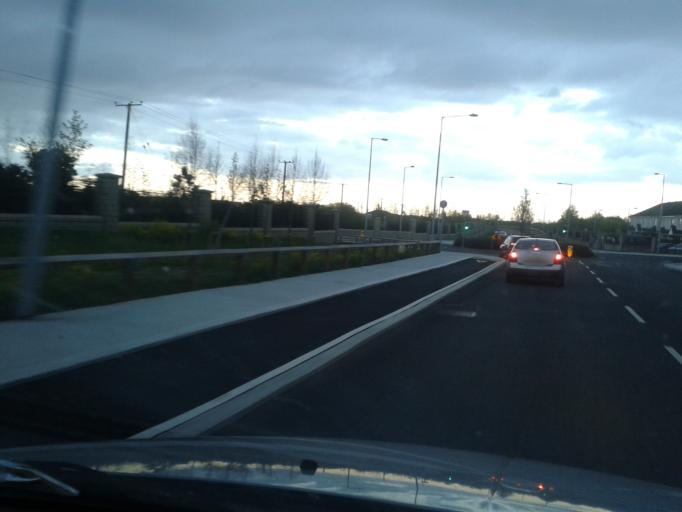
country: IE
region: Leinster
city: Kinsealy-Drinan
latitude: 53.4473
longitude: -6.2104
